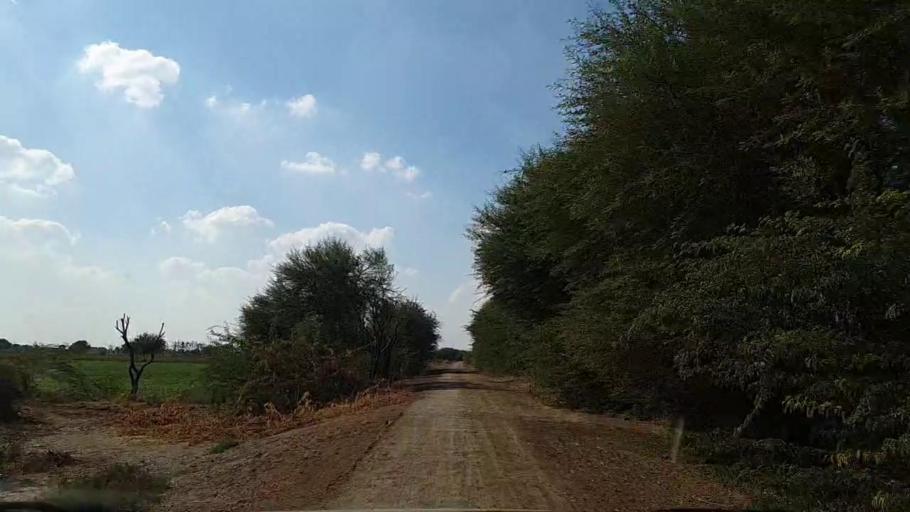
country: PK
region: Sindh
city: Pithoro
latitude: 25.6165
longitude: 69.3846
